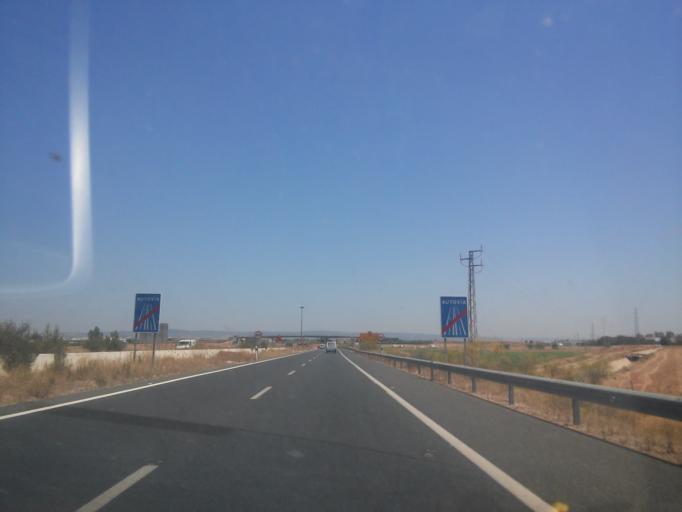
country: ES
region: Andalusia
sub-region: Provincia de Sevilla
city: La Rinconada
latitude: 37.4637
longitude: -5.9681
